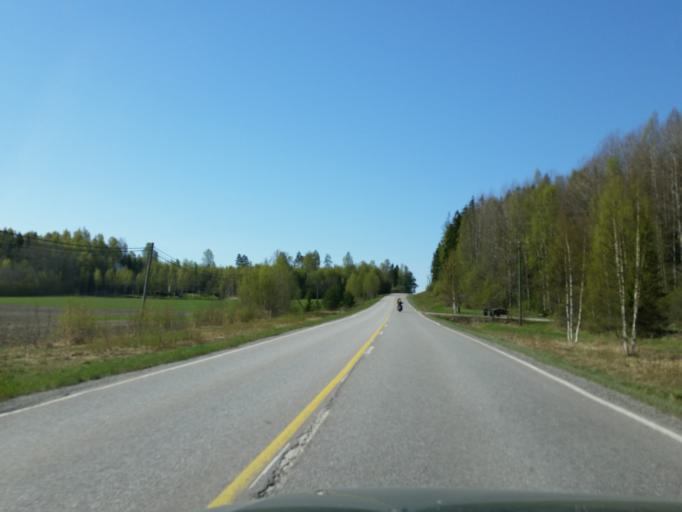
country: FI
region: Uusimaa
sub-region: Helsinki
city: Siuntio
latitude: 60.1931
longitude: 24.2497
